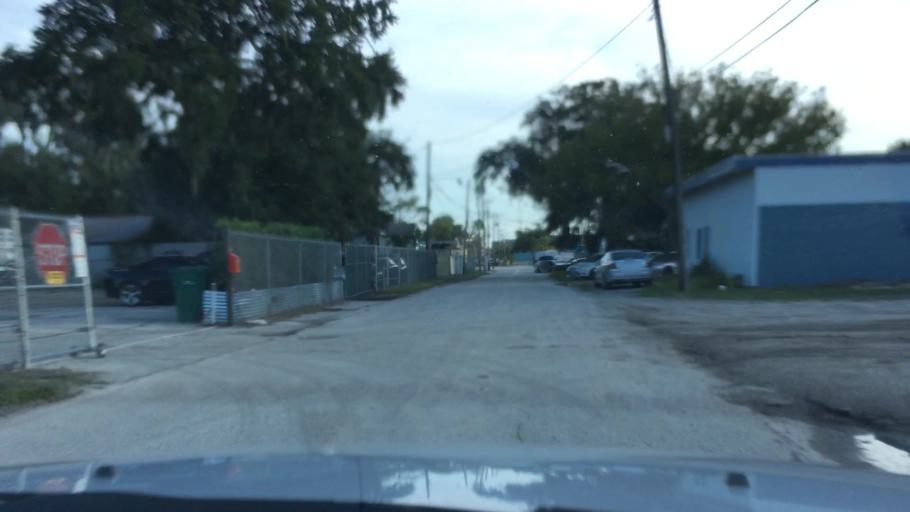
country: US
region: Florida
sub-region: Volusia County
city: Holly Hill
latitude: 29.2383
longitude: -81.0400
